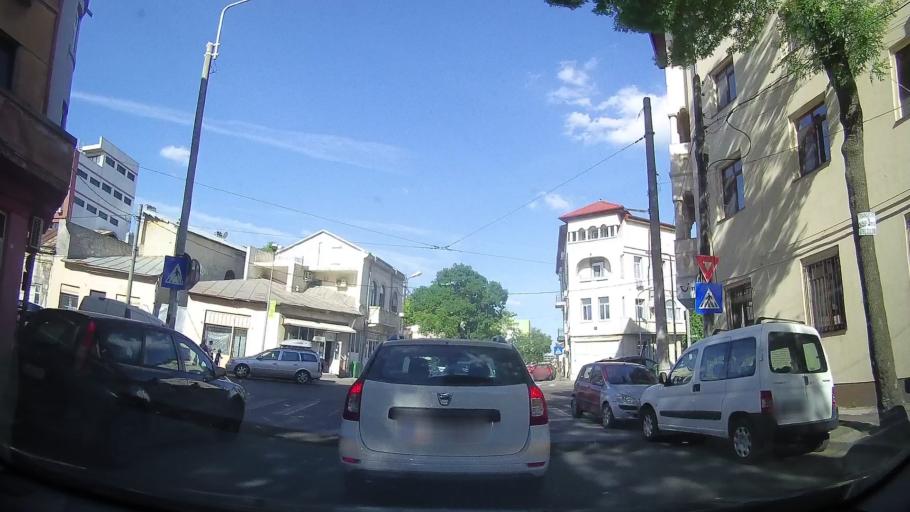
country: RO
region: Bucuresti
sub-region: Municipiul Bucuresti
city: Bucuresti
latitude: 44.4153
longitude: 26.1017
